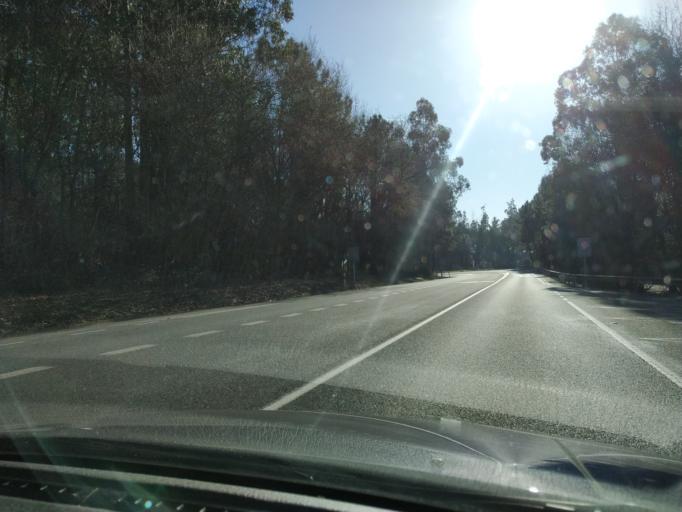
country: ES
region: Galicia
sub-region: Provincia da Coruna
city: Vedra
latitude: 42.7916
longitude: -8.4591
